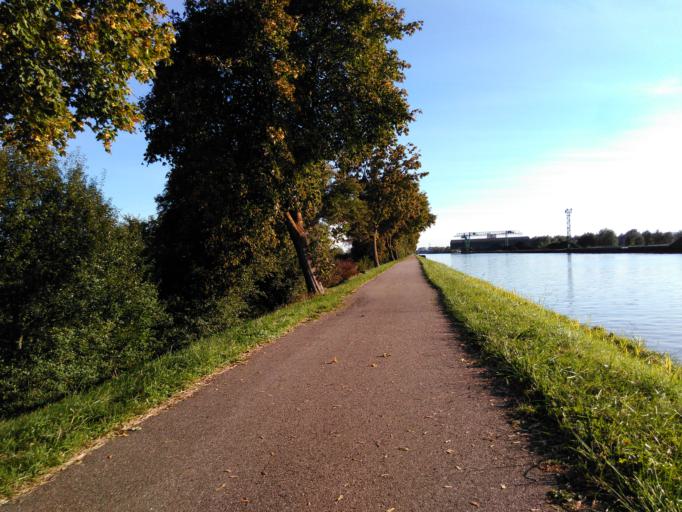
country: FR
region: Lorraine
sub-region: Departement de la Moselle
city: Bousse
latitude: 49.2764
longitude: 6.1821
